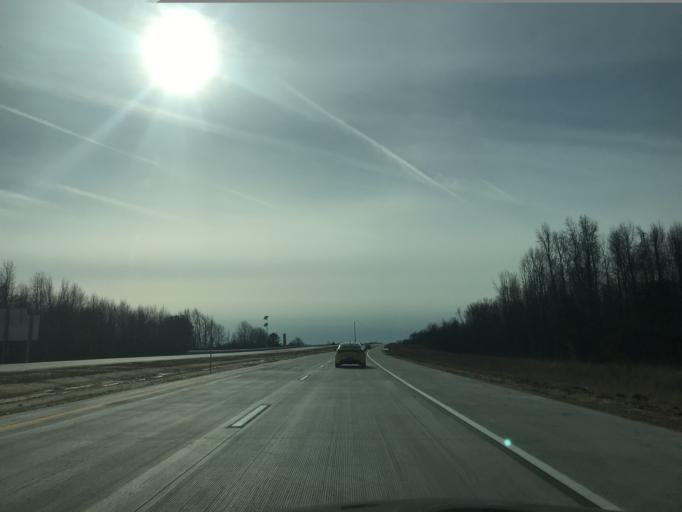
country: US
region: Delaware
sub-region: New Castle County
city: Middletown
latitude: 39.5118
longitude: -75.6918
